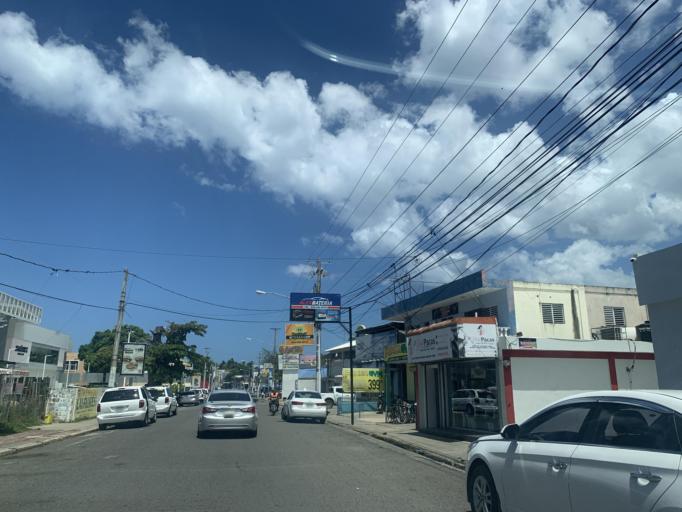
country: DO
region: Puerto Plata
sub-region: Puerto Plata
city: Puerto Plata
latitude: 19.7918
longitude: -70.6989
